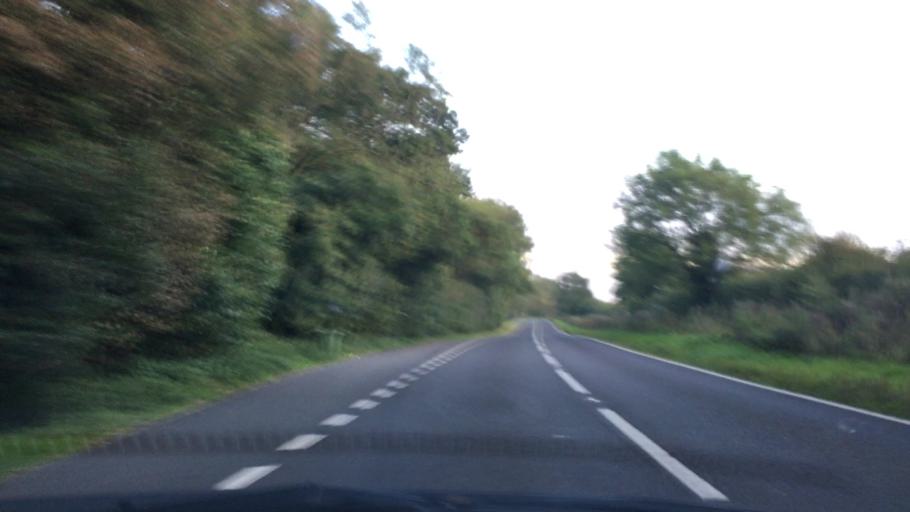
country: GB
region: England
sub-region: North East Lincolnshire
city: Wold Newton
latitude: 53.4731
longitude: -0.1119
